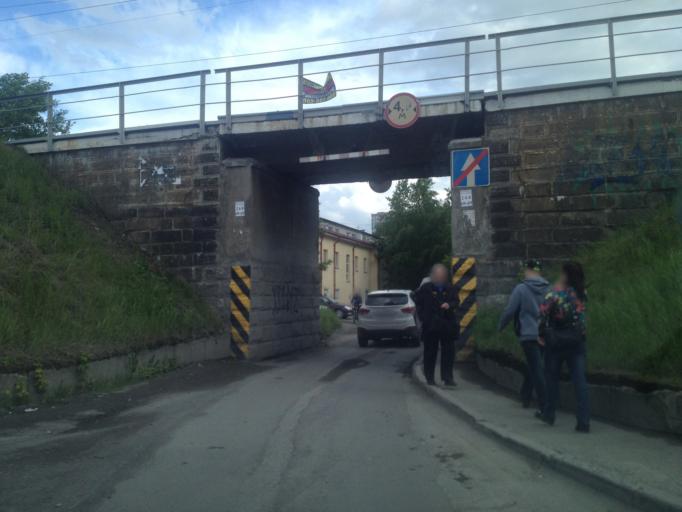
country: RU
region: Sverdlovsk
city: Yekaterinburg
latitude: 56.8586
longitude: 60.5804
